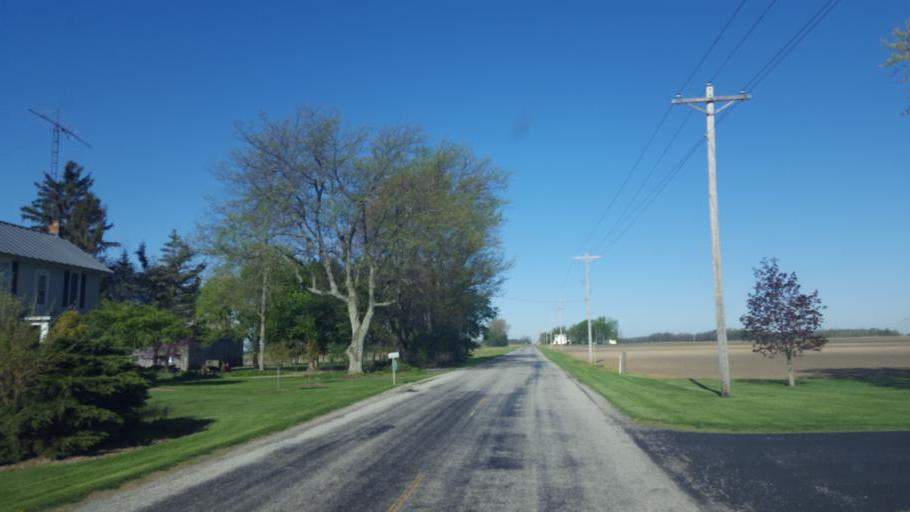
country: US
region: Ohio
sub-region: Crawford County
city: Bucyrus
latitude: 40.6742
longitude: -83.0060
